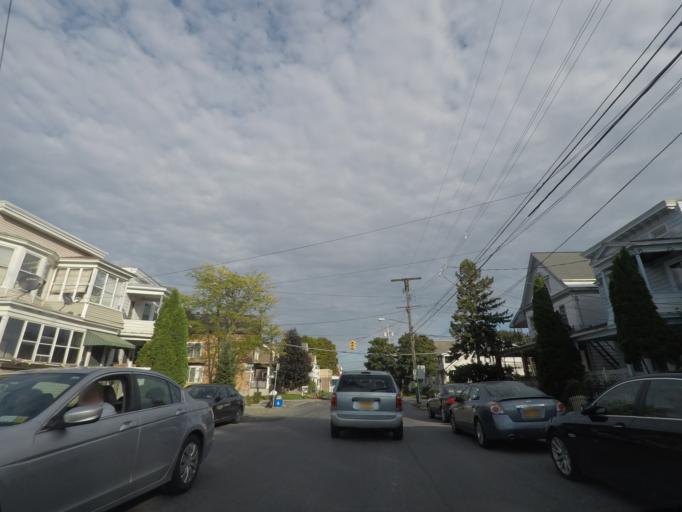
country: US
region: New York
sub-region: Albany County
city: Albany
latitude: 42.6392
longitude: -73.7791
